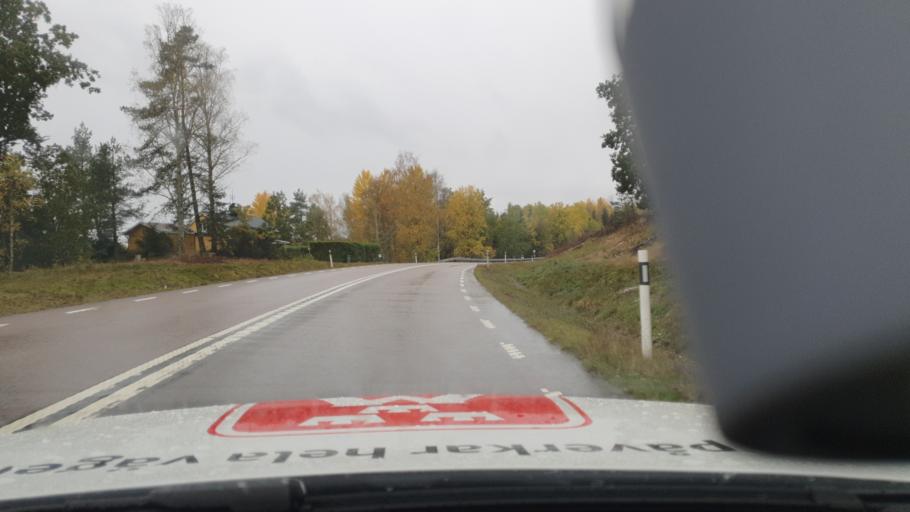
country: SE
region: Vaestra Goetaland
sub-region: Dals-Ed Kommun
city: Ed
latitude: 58.9227
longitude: 12.0309
